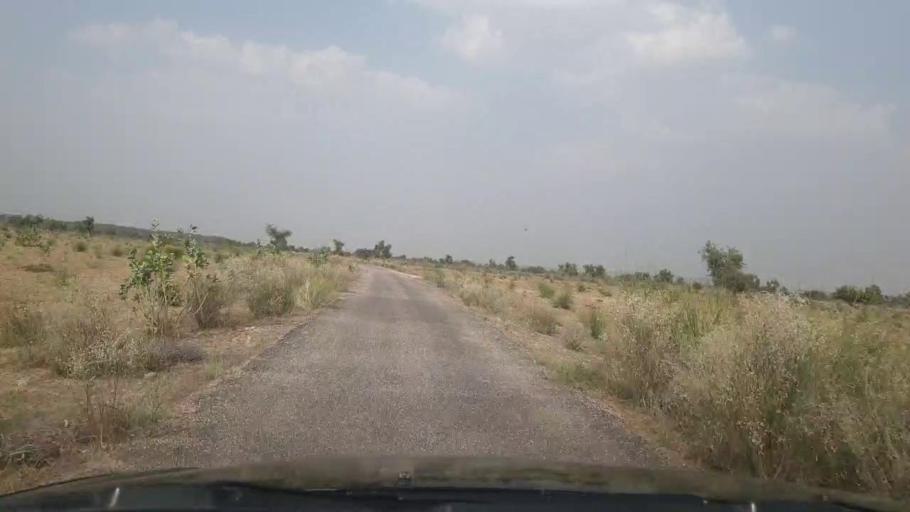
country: PK
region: Sindh
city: Islamkot
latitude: 24.9019
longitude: 70.5576
